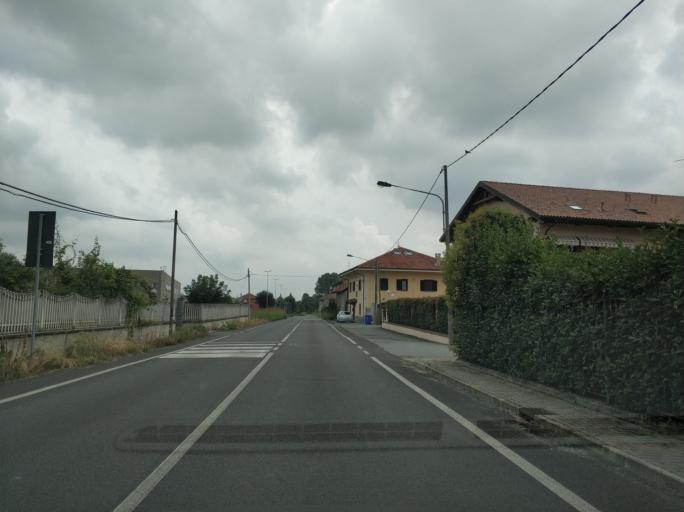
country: IT
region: Piedmont
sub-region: Provincia di Torino
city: San Maurizio
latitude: 45.1917
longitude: 7.6201
